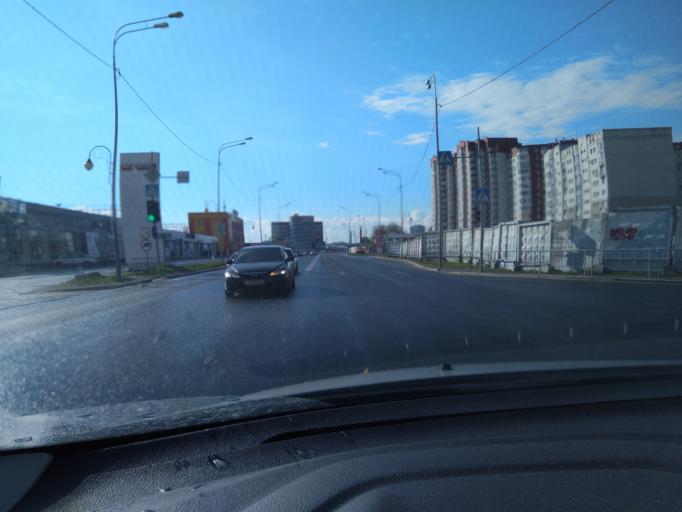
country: RU
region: Tjumen
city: Tyumen
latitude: 57.1390
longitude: 65.5451
